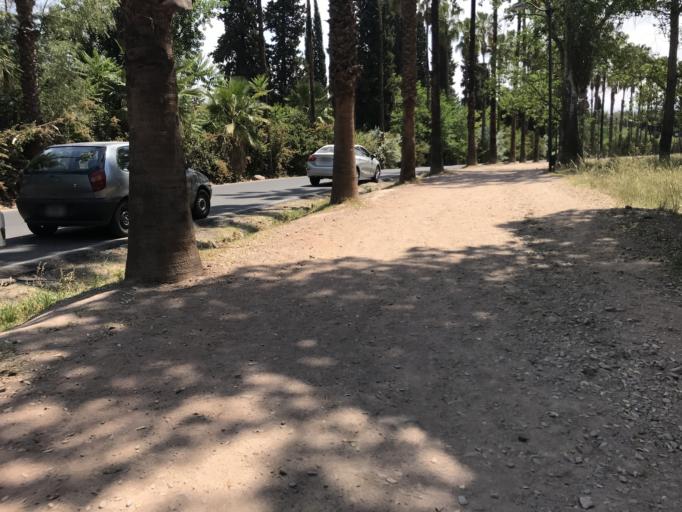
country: AR
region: Mendoza
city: Mendoza
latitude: -32.8943
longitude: -68.8689
